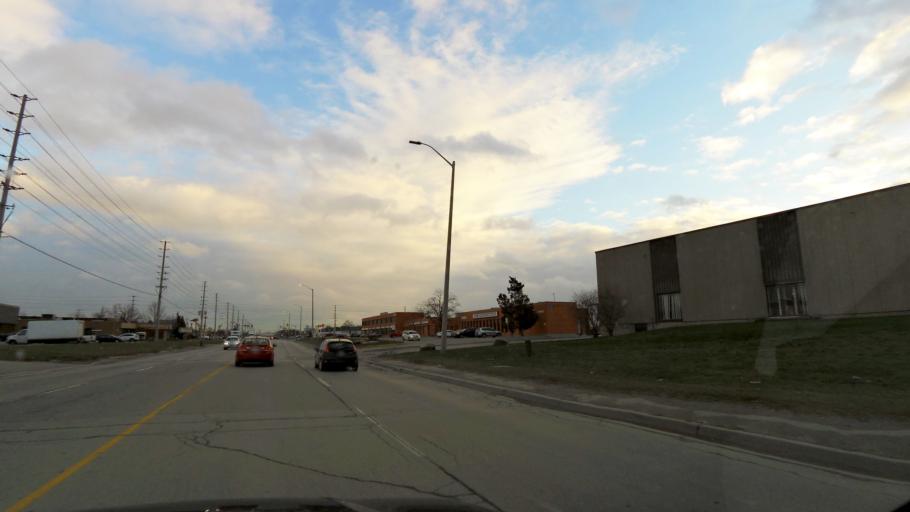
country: CA
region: Ontario
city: Etobicoke
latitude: 43.7007
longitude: -79.6615
